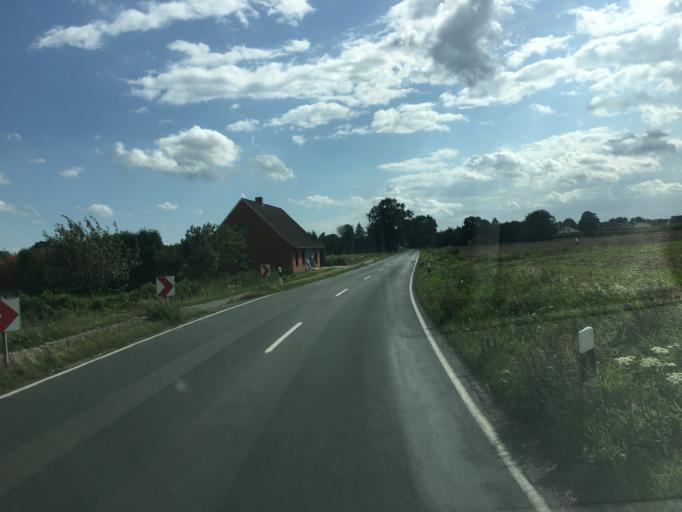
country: DE
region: Lower Saxony
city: Friesoythe
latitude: 53.0390
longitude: 7.8576
